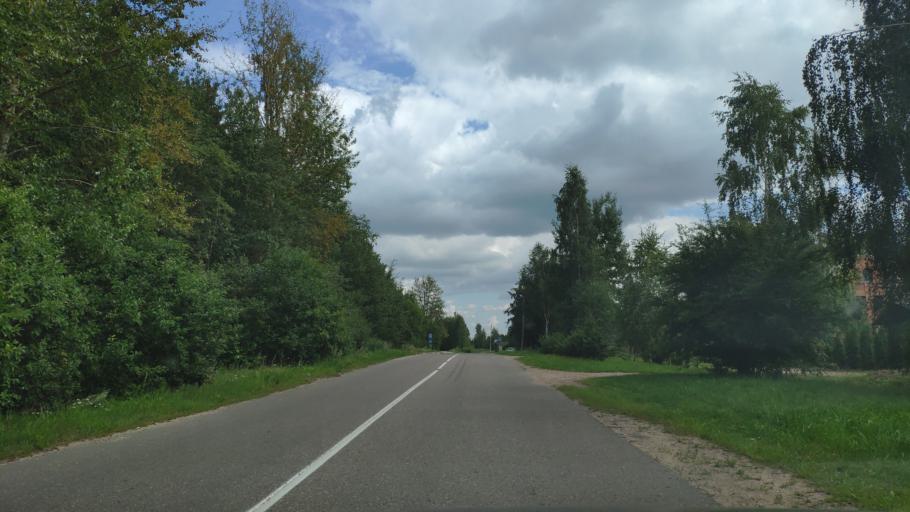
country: BY
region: Minsk
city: Khatsyezhyna
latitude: 53.8755
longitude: 27.2943
